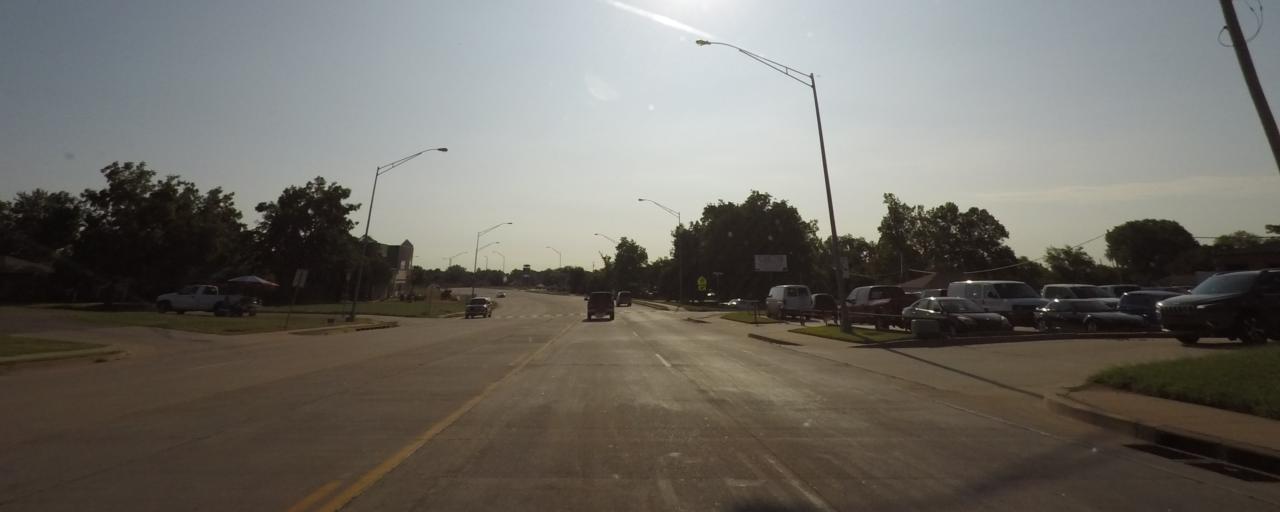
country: US
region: Oklahoma
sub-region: McClain County
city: Blanchard
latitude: 35.1379
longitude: -97.6565
